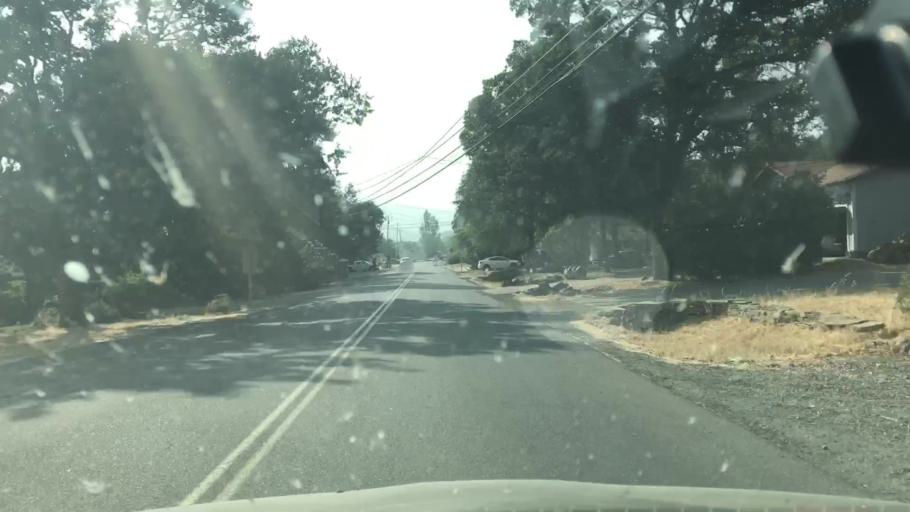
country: US
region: California
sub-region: Lake County
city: Hidden Valley Lake
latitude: 38.8027
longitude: -122.5594
